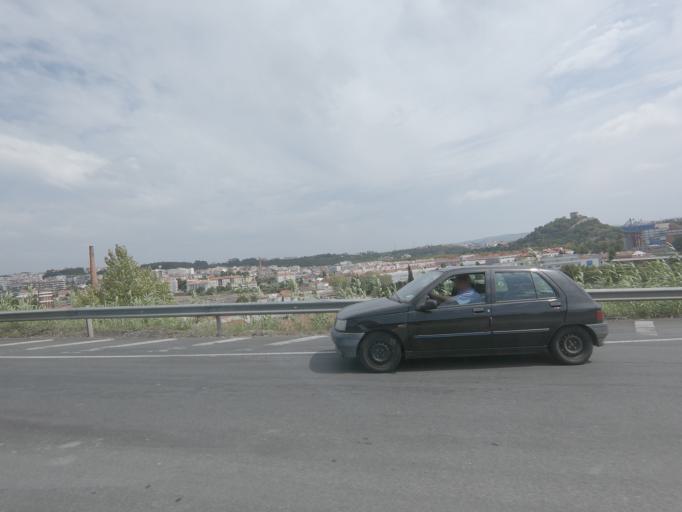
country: PT
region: Leiria
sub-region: Leiria
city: Leiria
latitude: 39.7558
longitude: -8.8145
